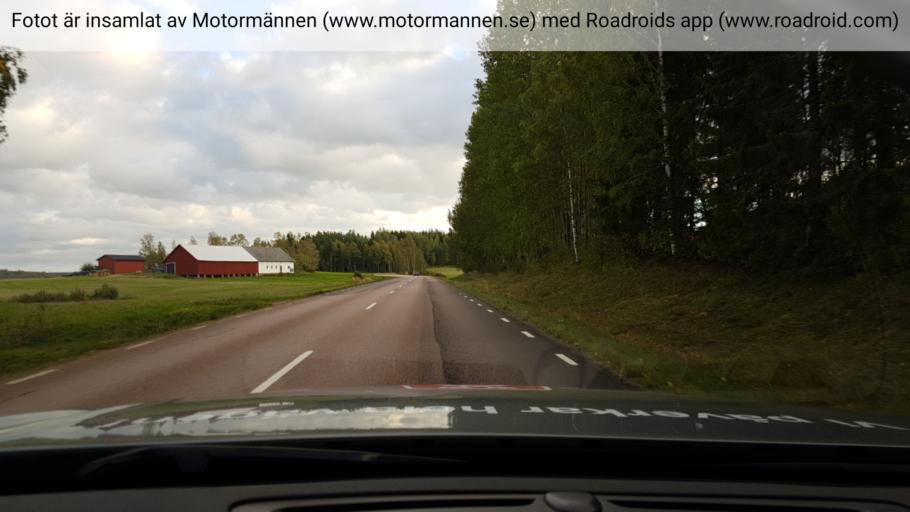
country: SE
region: Vaermland
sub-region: Karlstads Kommun
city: Molkom
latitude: 59.4564
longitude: 13.8257
